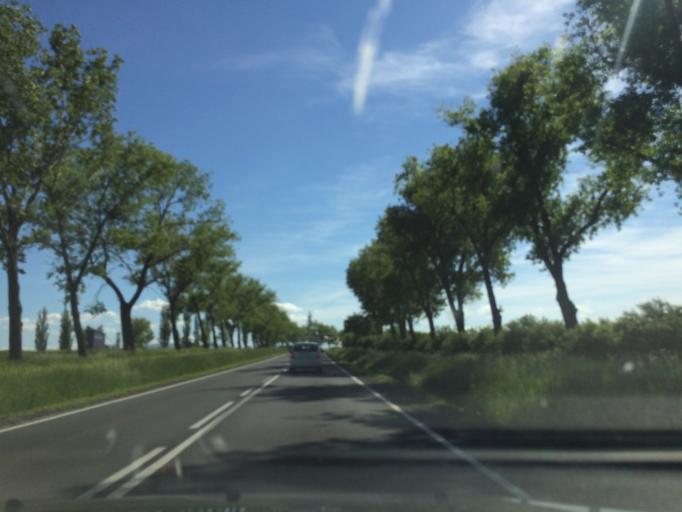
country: PL
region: Lower Silesian Voivodeship
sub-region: Powiat swidnicki
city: Swidnica
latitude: 50.8620
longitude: 16.5562
